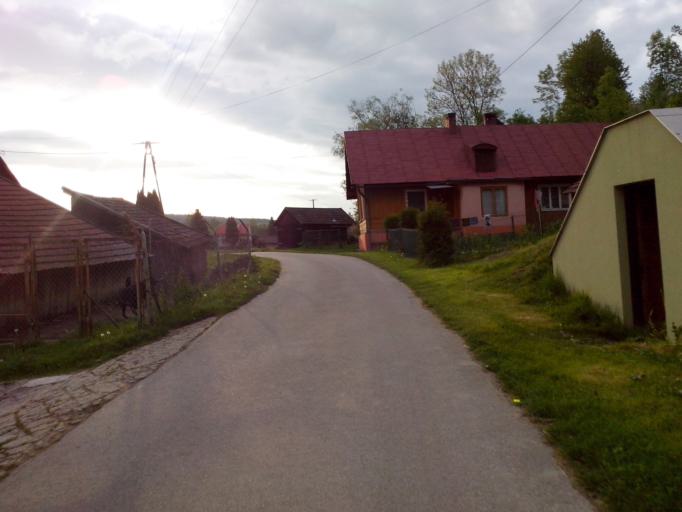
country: PL
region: Subcarpathian Voivodeship
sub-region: Powiat strzyzowski
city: Jawornik
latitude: 49.8228
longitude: 21.8389
